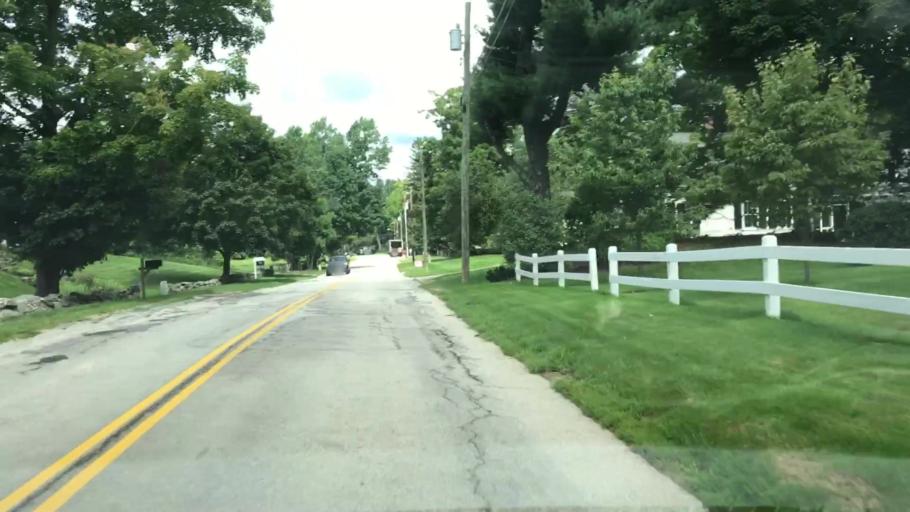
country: US
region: New Hampshire
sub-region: Hillsborough County
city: Milford
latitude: 42.8680
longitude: -71.6238
